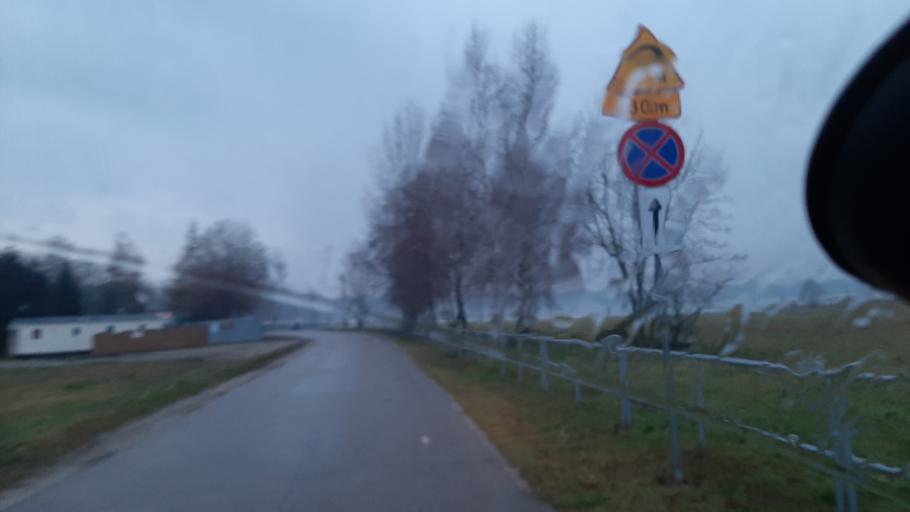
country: PL
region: Lublin Voivodeship
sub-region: Powiat lubartowski
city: Firlej
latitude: 51.5584
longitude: 22.5231
